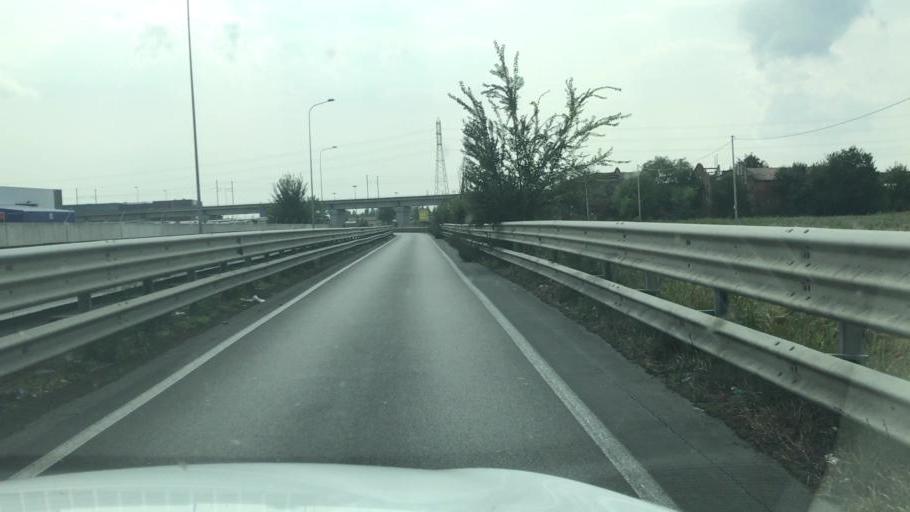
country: IT
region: Emilia-Romagna
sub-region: Provincia di Parma
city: Baganzola
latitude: 44.8442
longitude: 10.3405
